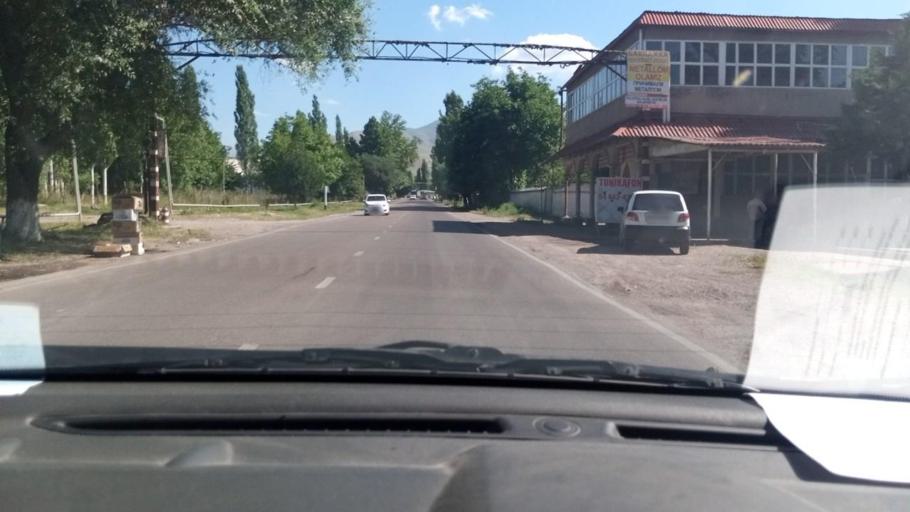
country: UZ
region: Toshkent
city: Angren
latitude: 41.0357
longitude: 70.0931
